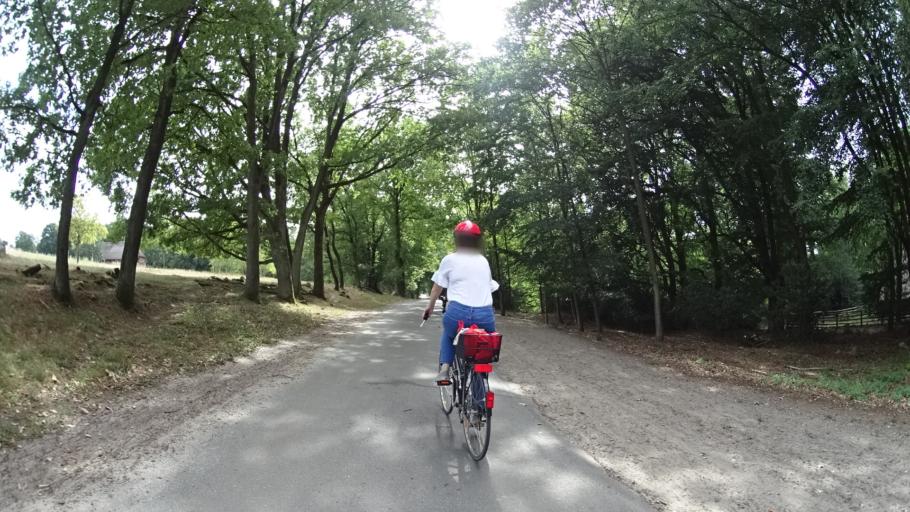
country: DE
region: Lower Saxony
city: Undeloh
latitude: 53.1661
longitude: 9.9654
